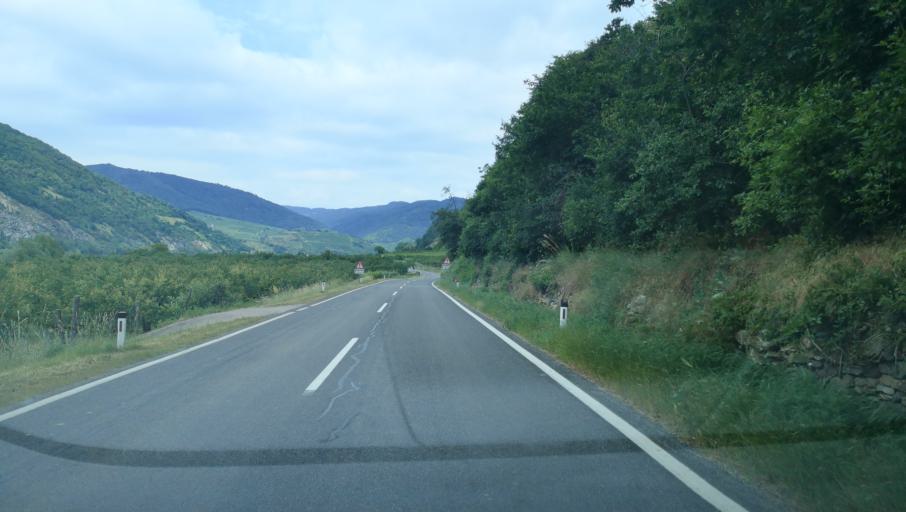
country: AT
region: Lower Austria
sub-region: Politischer Bezirk Krems
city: Spitz
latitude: 48.3381
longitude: 15.4104
